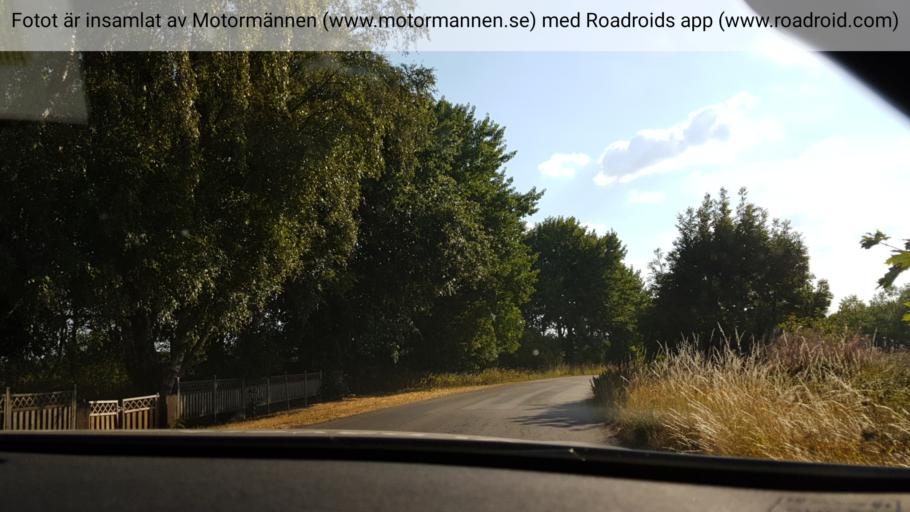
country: SE
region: Vaestra Goetaland
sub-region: Skovde Kommun
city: Stopen
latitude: 58.4869
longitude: 13.7700
